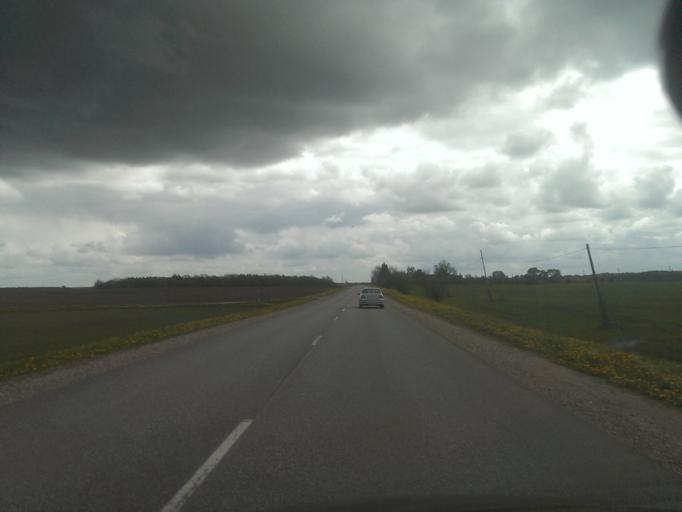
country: LV
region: Kuldigas Rajons
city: Kuldiga
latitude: 56.9928
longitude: 21.9101
